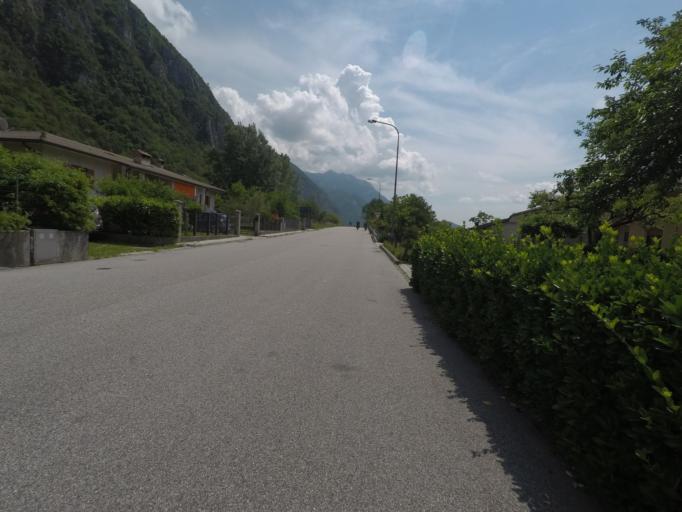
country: IT
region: Friuli Venezia Giulia
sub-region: Provincia di Udine
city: Venzone
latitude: 46.3677
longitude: 13.1339
